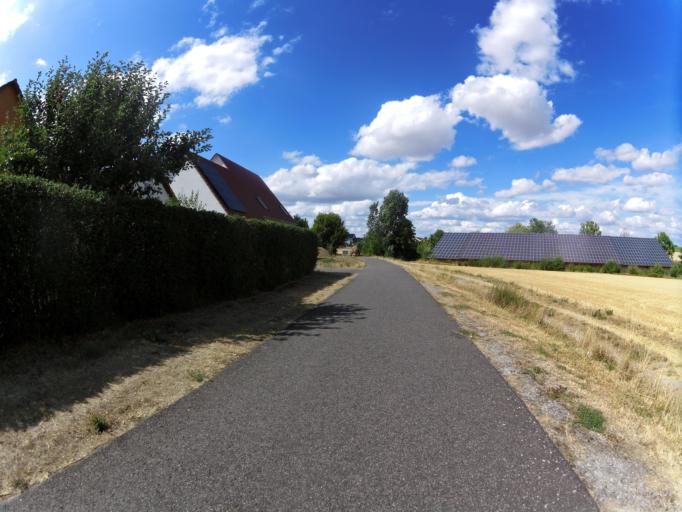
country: DE
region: Bavaria
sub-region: Regierungsbezirk Unterfranken
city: Sonderhofen
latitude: 49.5953
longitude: 10.0058
